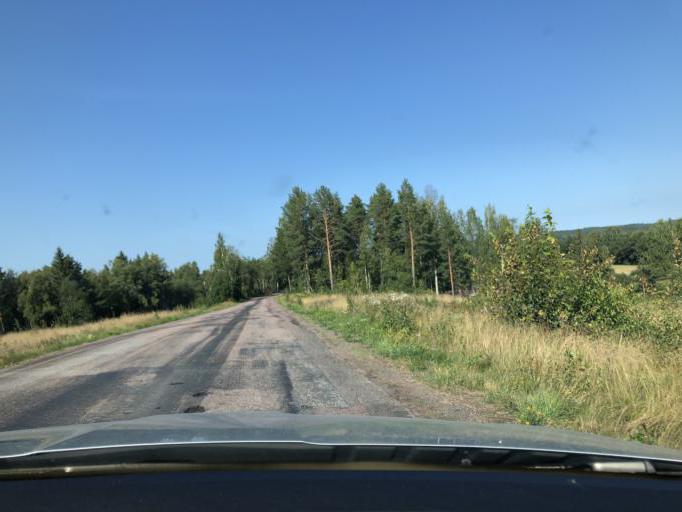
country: SE
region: Dalarna
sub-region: Hedemora Kommun
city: Hedemora
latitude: 60.3322
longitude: 15.9191
